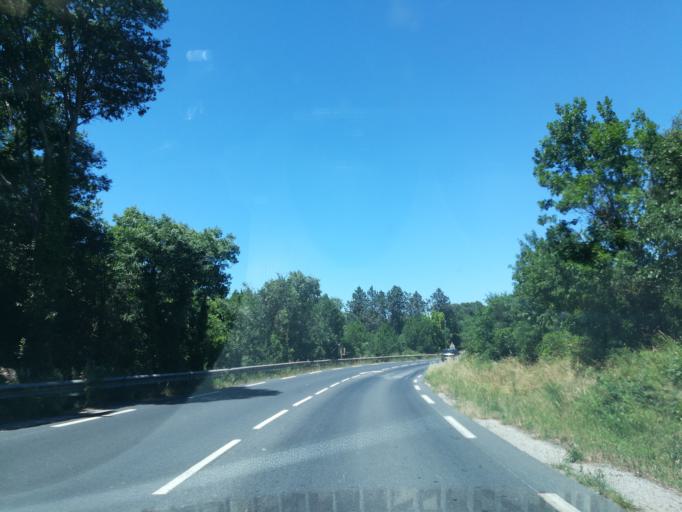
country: FR
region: Languedoc-Roussillon
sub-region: Departement des Pyrenees-Orientales
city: el Volo
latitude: 42.5053
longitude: 2.8235
